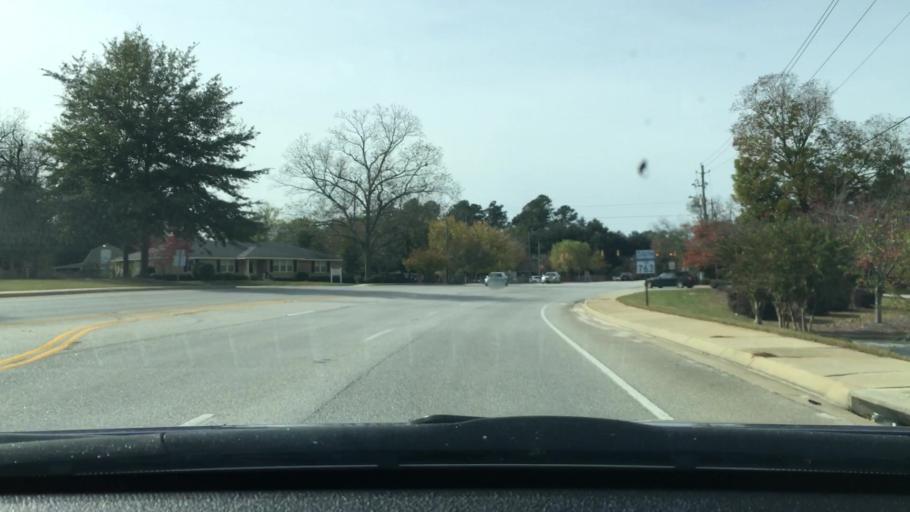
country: US
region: South Carolina
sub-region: Sumter County
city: South Sumter
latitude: 33.9143
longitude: -80.3862
